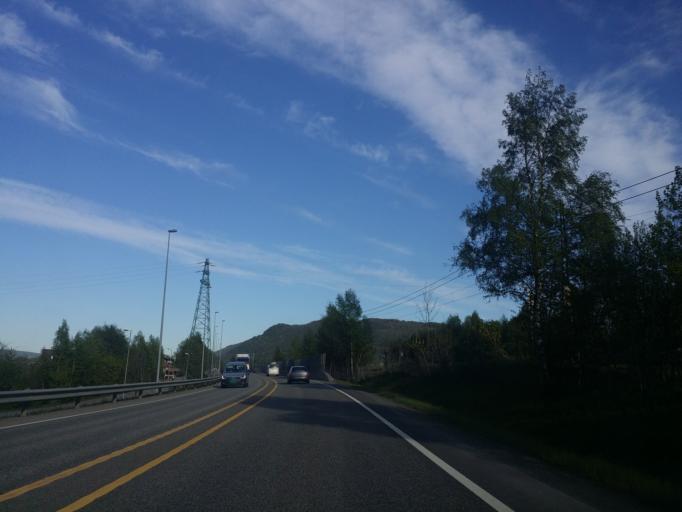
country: NO
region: Buskerud
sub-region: Nedre Eiker
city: Mjondalen
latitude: 59.7538
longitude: 9.9910
